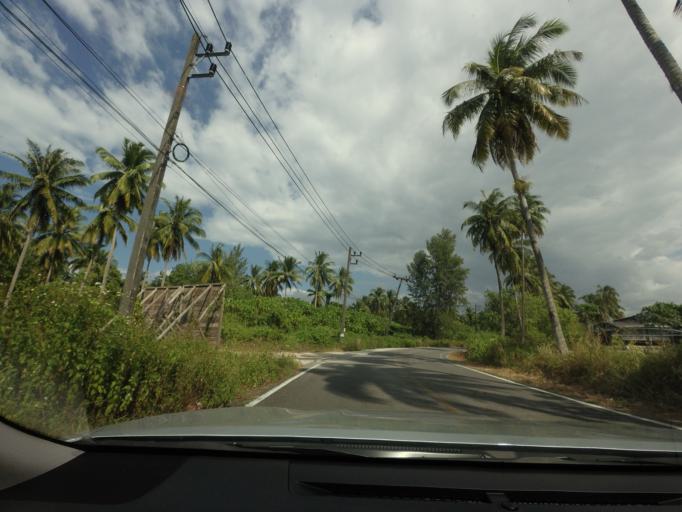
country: TH
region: Phangnga
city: Ban Khao Lak
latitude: 8.7291
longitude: 98.2341
